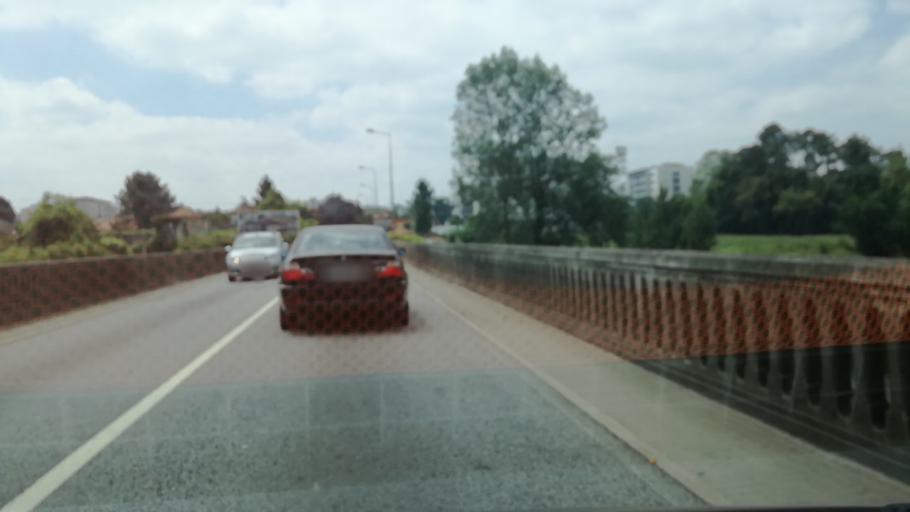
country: PT
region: Porto
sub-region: Trofa
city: Bougado
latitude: 41.3453
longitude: -8.5564
